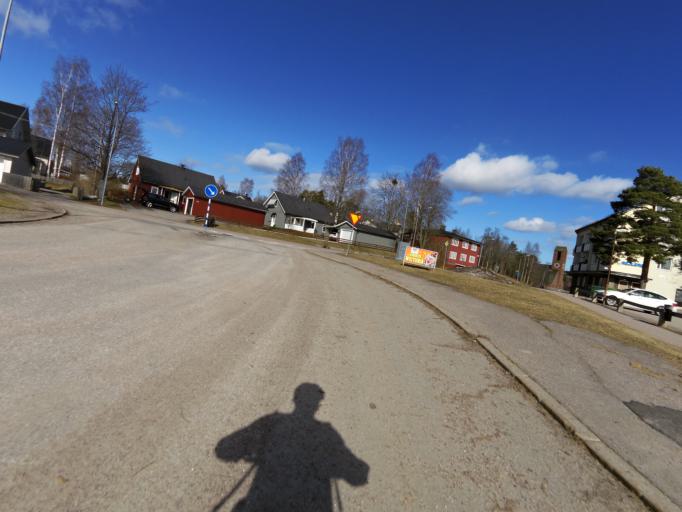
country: SE
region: Gaevleborg
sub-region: Hofors Kommun
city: Hofors
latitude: 60.5489
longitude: 16.2871
